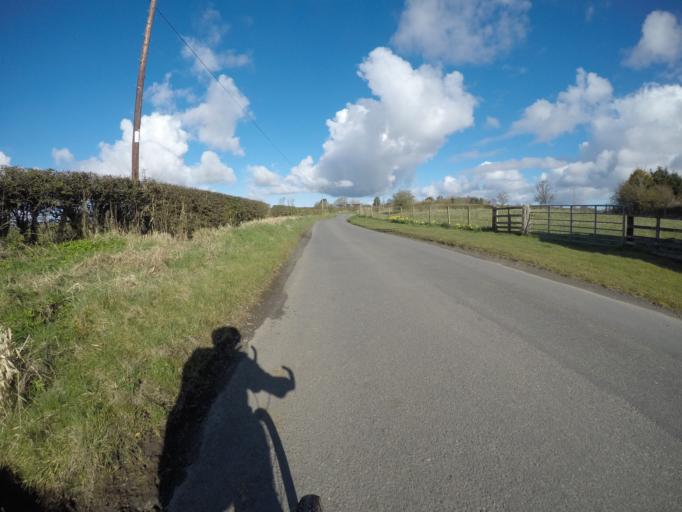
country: GB
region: Scotland
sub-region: North Ayrshire
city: Irvine
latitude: 55.6556
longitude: -4.6534
